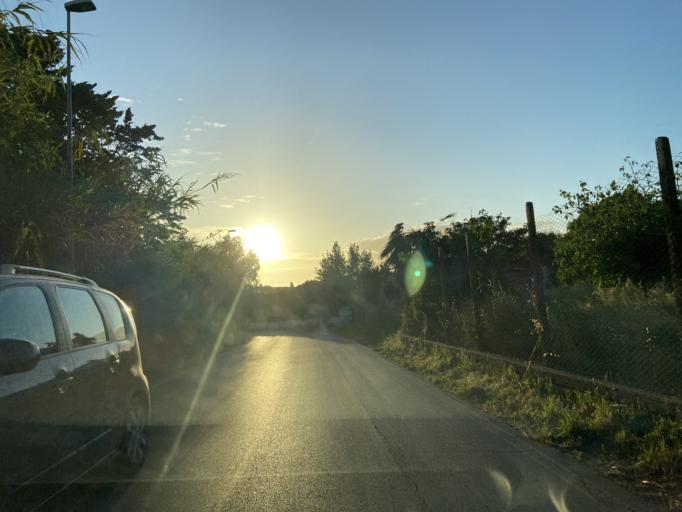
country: IT
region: Latium
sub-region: Citta metropolitana di Roma Capitale
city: Civitavecchia
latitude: 42.0781
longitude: 11.8216
